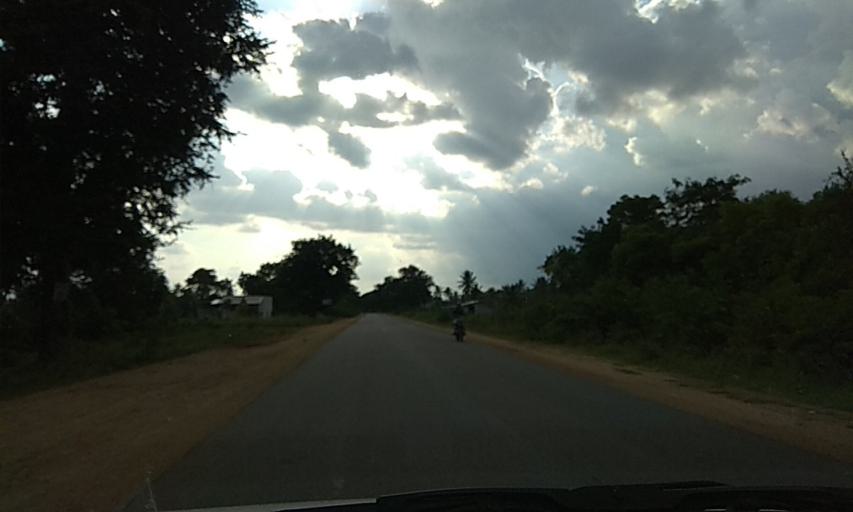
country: IN
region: Karnataka
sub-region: Chamrajnagar
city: Gundlupet
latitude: 11.8110
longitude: 76.7315
